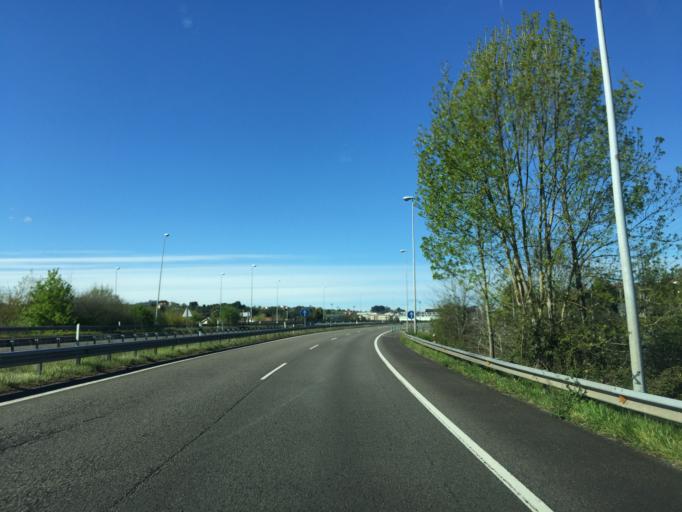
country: ES
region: Asturias
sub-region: Province of Asturias
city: Gijon
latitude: 43.5159
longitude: -5.6572
